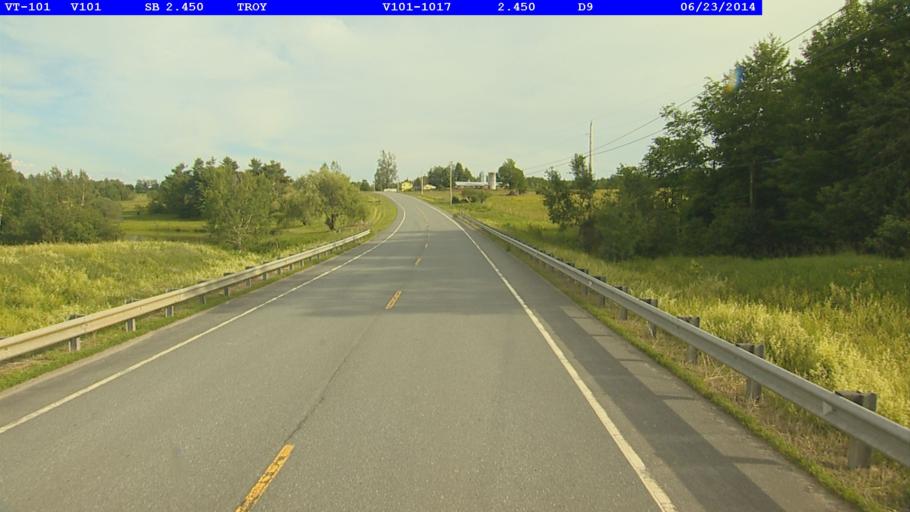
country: US
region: Vermont
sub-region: Orleans County
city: Newport
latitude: 44.9379
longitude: -72.4122
